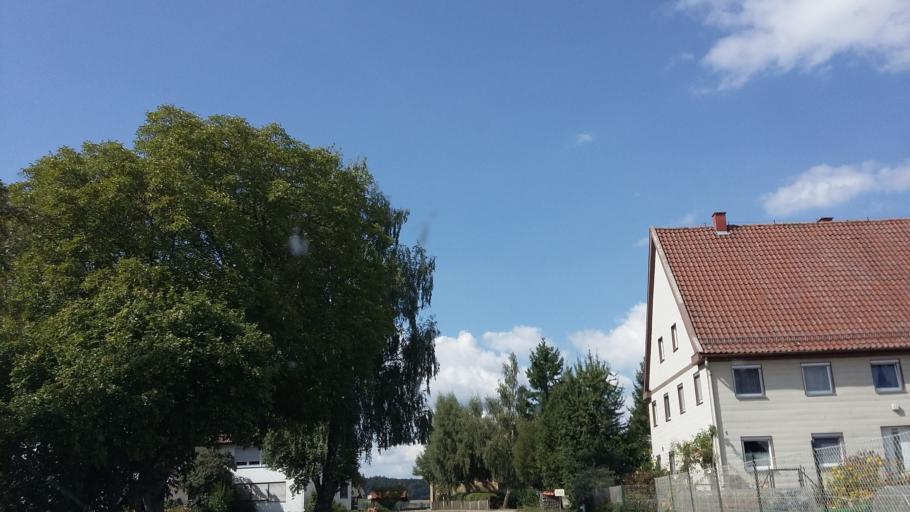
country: DE
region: Bavaria
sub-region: Swabia
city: Holzheim
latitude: 48.3536
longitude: 10.1152
